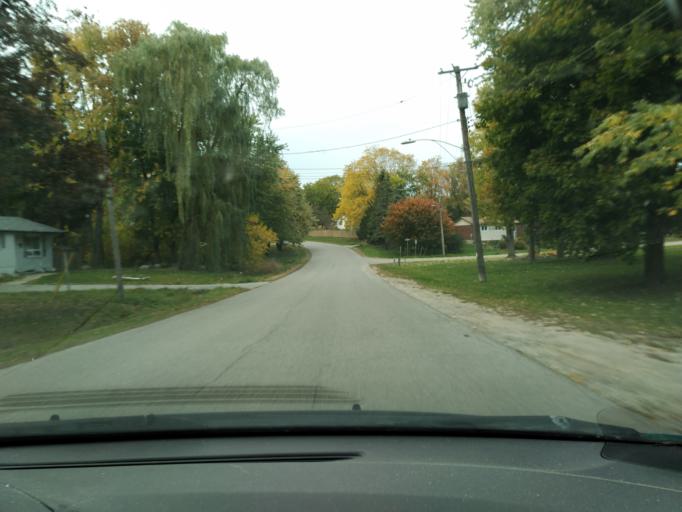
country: CA
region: Ontario
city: Bradford West Gwillimbury
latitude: 44.0877
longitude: -79.6785
